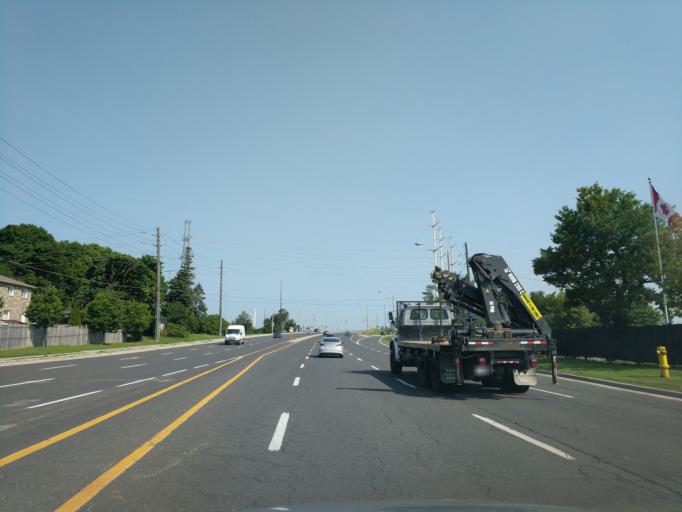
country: CA
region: Ontario
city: Scarborough
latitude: 43.7927
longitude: -79.1958
